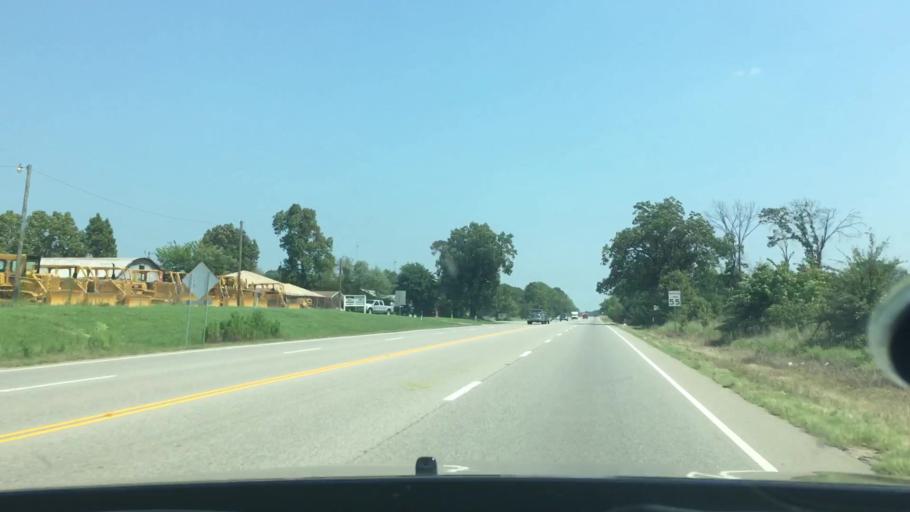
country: US
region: Oklahoma
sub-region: Atoka County
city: Atoka
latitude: 34.3329
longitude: -96.1595
